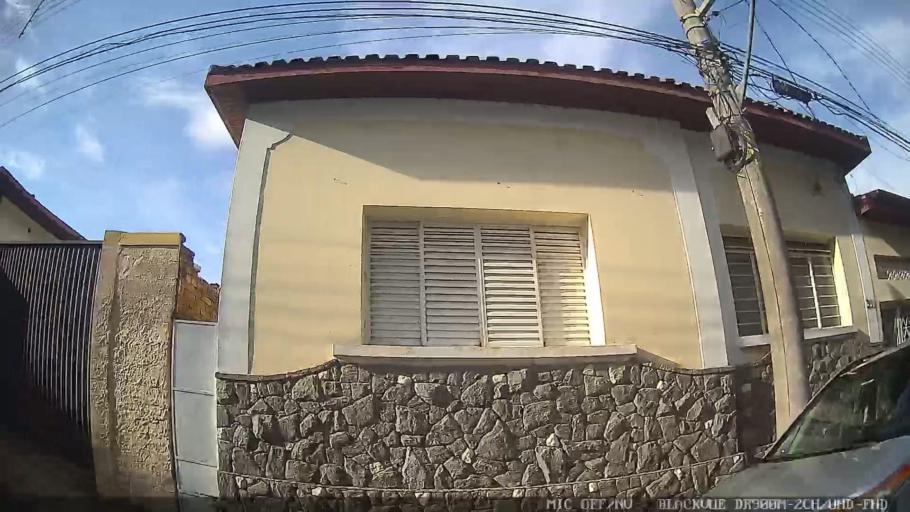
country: BR
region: Sao Paulo
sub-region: Tiete
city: Tiete
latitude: -23.0985
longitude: -47.7150
